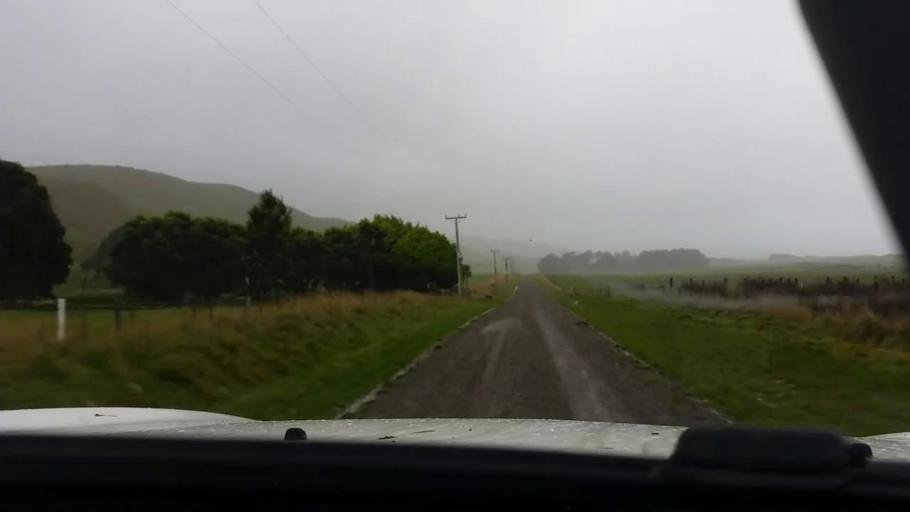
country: NZ
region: Wellington
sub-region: Masterton District
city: Masterton
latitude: -41.2572
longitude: 175.9040
